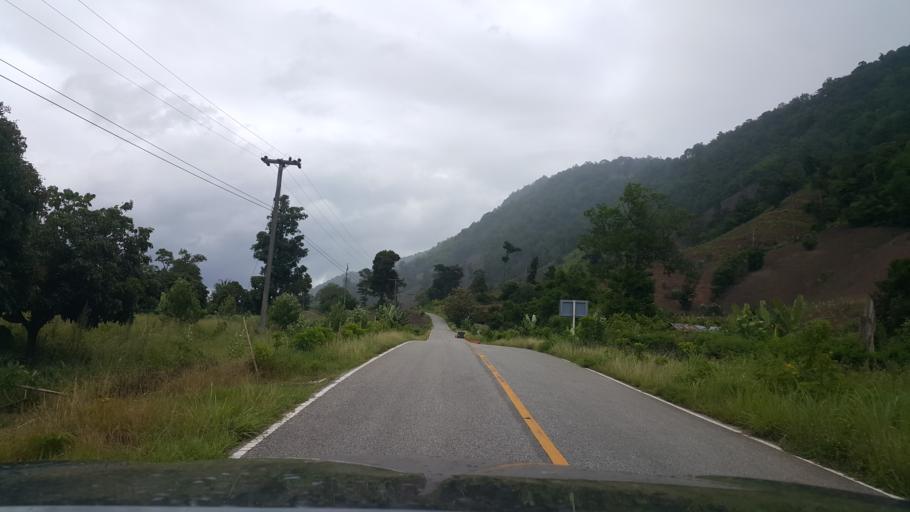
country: TH
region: Loei
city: Na Haeo
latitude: 17.5569
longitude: 100.8448
